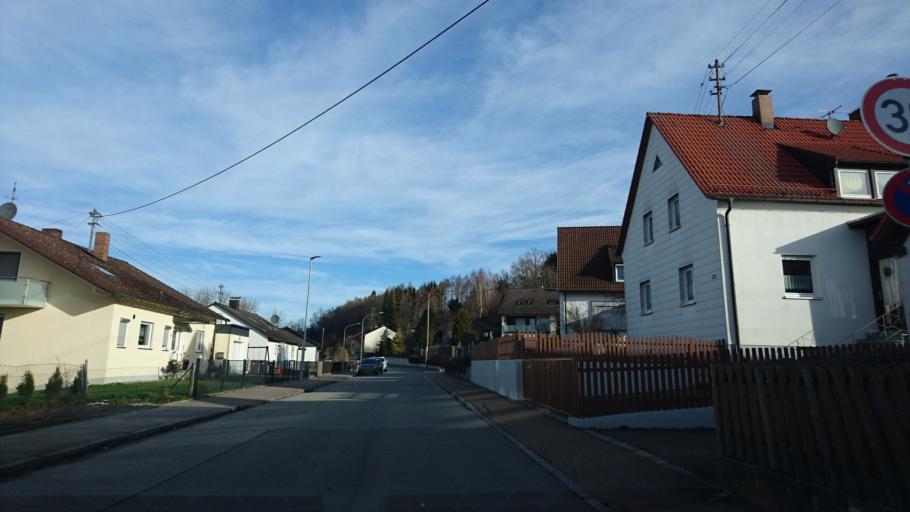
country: DE
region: Bavaria
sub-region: Swabia
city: Welden
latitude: 48.4611
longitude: 10.6603
